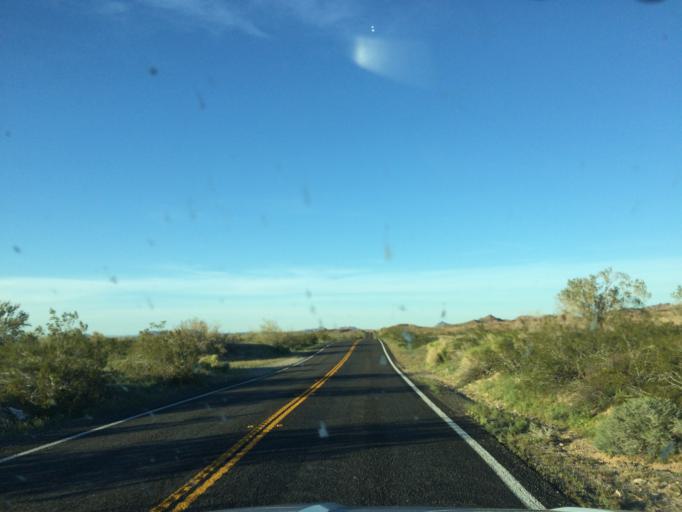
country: US
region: California
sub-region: Riverside County
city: Mesa Verde
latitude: 33.1813
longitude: -114.8651
